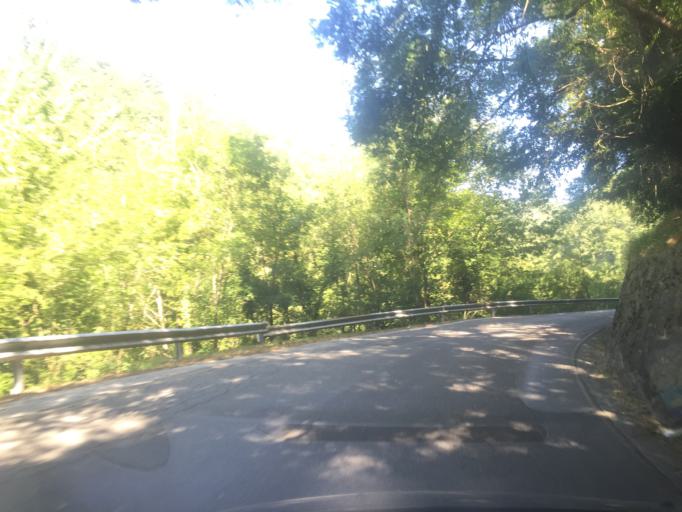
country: IT
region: Tuscany
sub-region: Provincia di Lucca
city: Careggine
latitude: 44.1312
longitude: 10.3096
